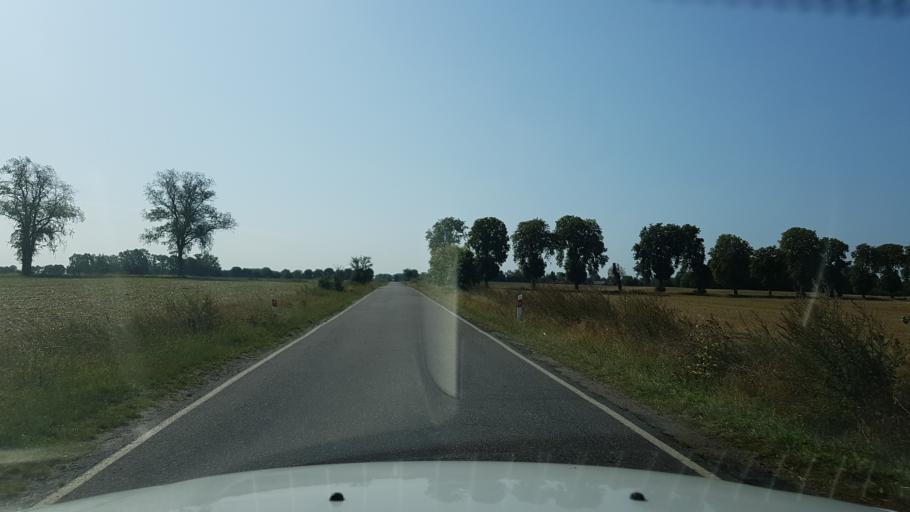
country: PL
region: West Pomeranian Voivodeship
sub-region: Powiat stargardzki
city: Dolice
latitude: 53.1516
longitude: 15.2413
